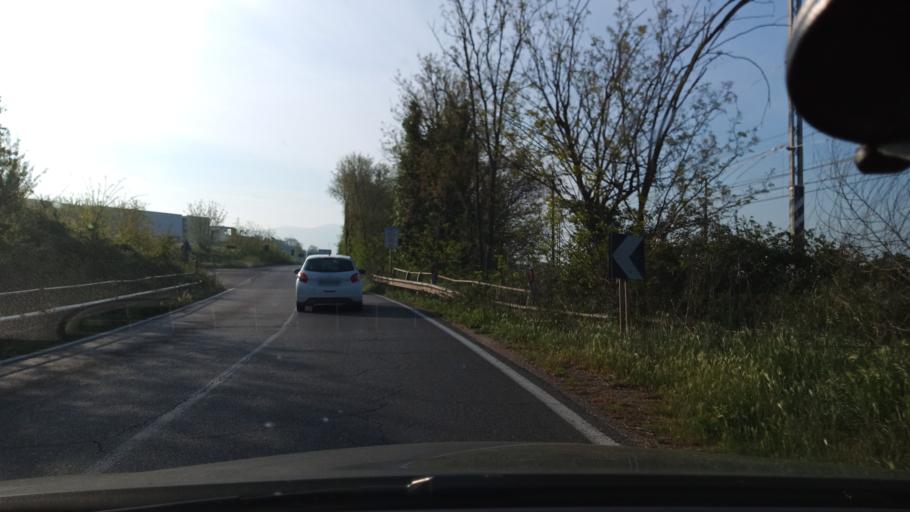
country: IT
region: Latium
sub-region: Citta metropolitana di Roma Capitale
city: Fiano Romano
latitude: 42.1687
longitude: 12.6379
